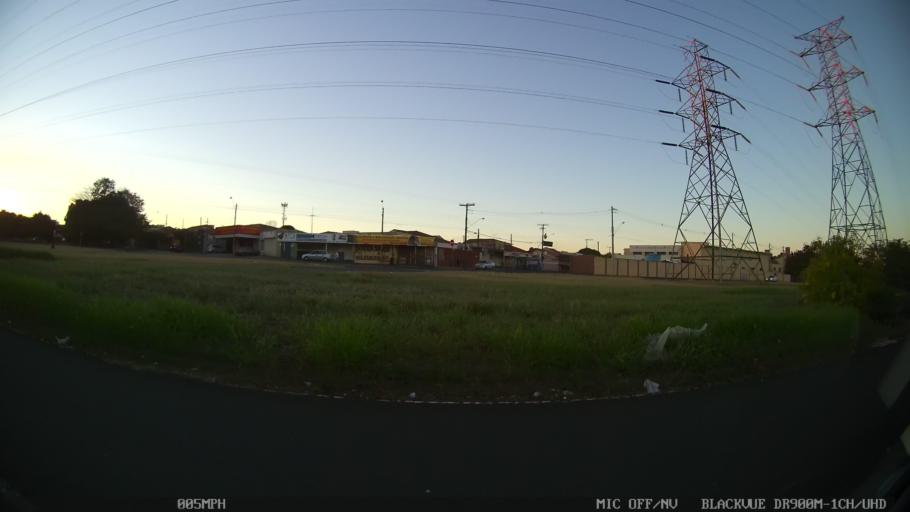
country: BR
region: Sao Paulo
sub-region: Sao Jose Do Rio Preto
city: Sao Jose do Rio Preto
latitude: -20.8443
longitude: -49.3795
